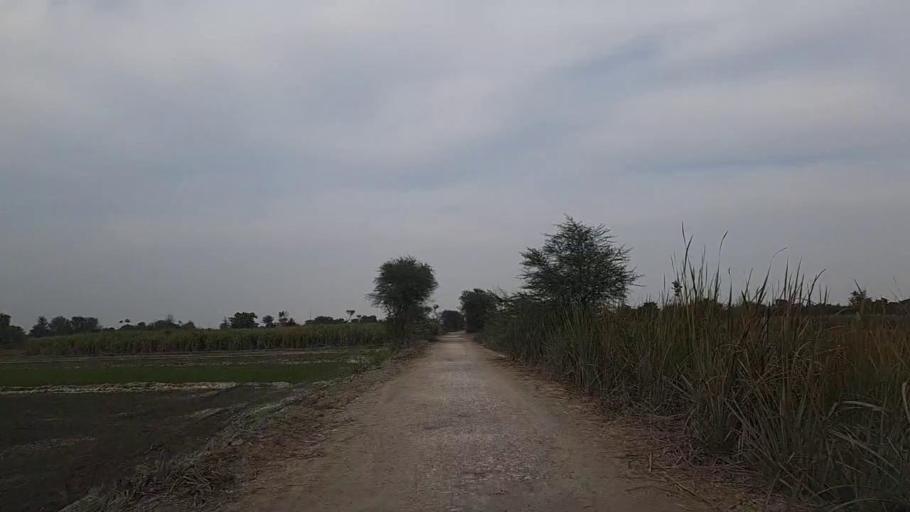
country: PK
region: Sindh
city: Daur
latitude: 26.5166
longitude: 68.4161
